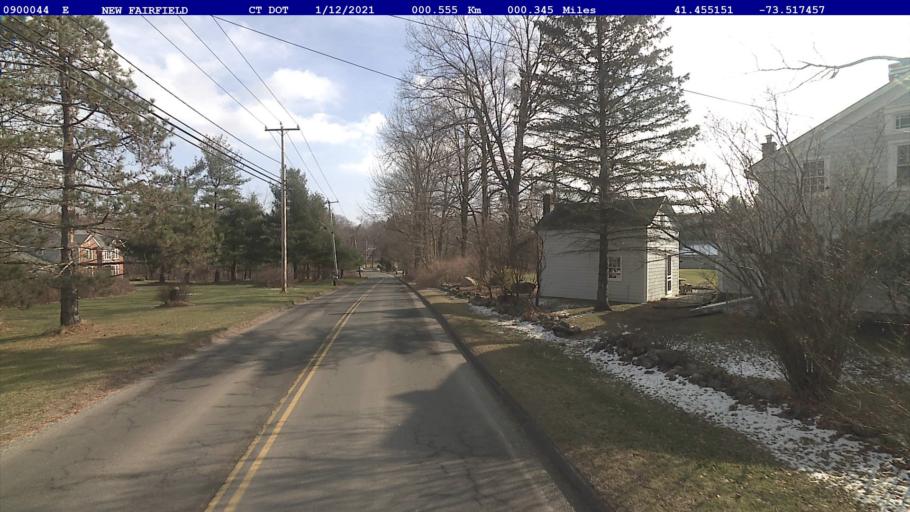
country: US
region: New York
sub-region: Putnam County
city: Putnam Lake
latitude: 41.4551
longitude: -73.5175
